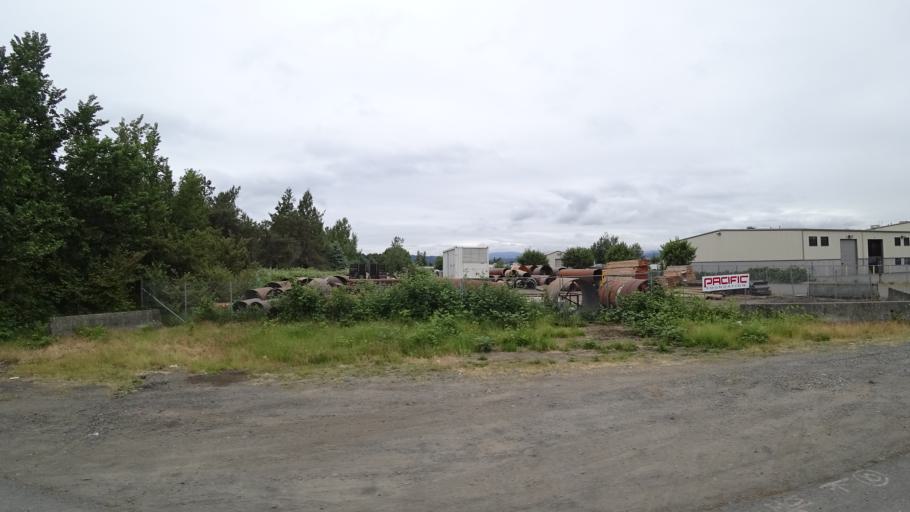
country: US
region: Oregon
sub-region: Multnomah County
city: Wood Village
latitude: 45.5427
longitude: -122.4178
